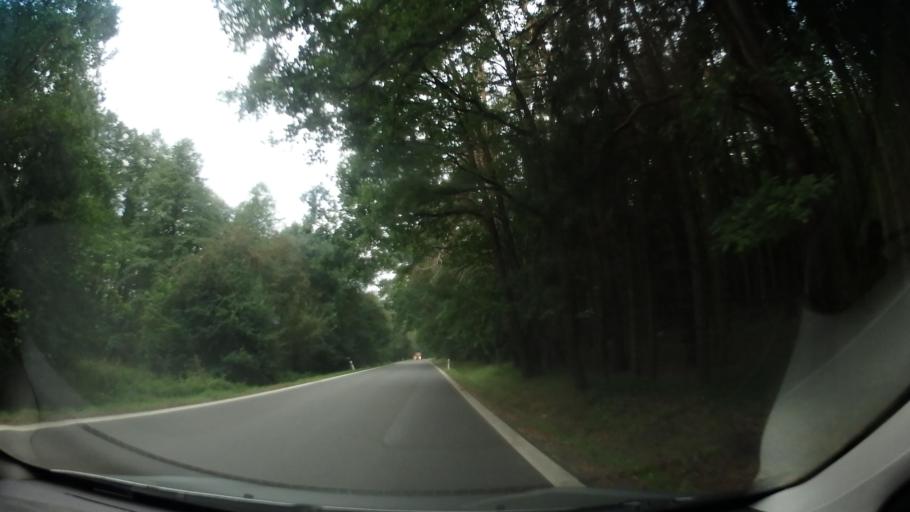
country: CZ
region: Central Bohemia
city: Bystrice
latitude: 49.7604
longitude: 14.6293
